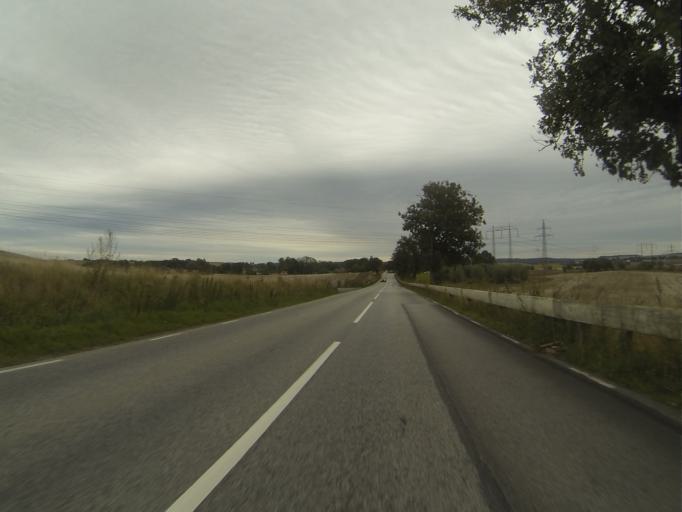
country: SE
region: Skane
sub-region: Malmo
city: Oxie
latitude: 55.5815
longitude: 13.1411
